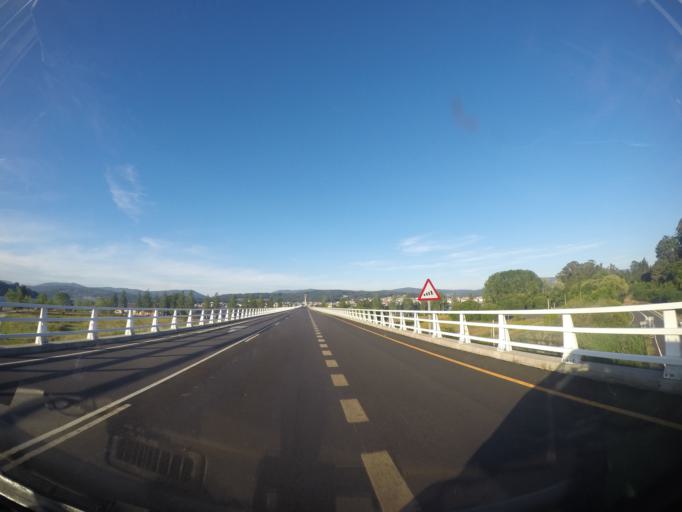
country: ES
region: Galicia
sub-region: Provincia da Coruna
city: Noia
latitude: 42.7890
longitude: -8.9113
